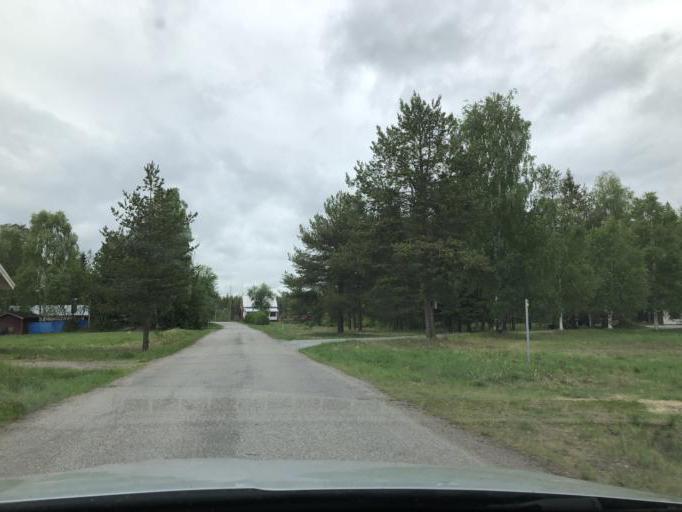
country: SE
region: Norrbotten
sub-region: Pitea Kommun
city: Roknas
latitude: 65.3771
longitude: 21.2786
